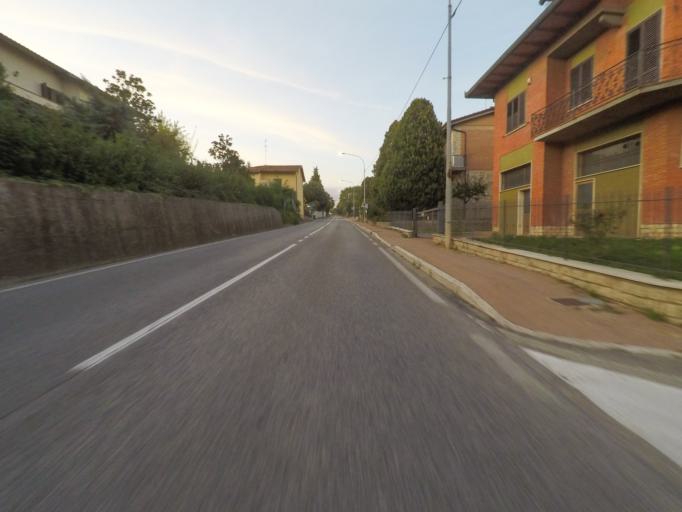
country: IT
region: Tuscany
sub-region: Provincia di Siena
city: Torrita di Siena
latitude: 43.1720
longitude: 11.7742
